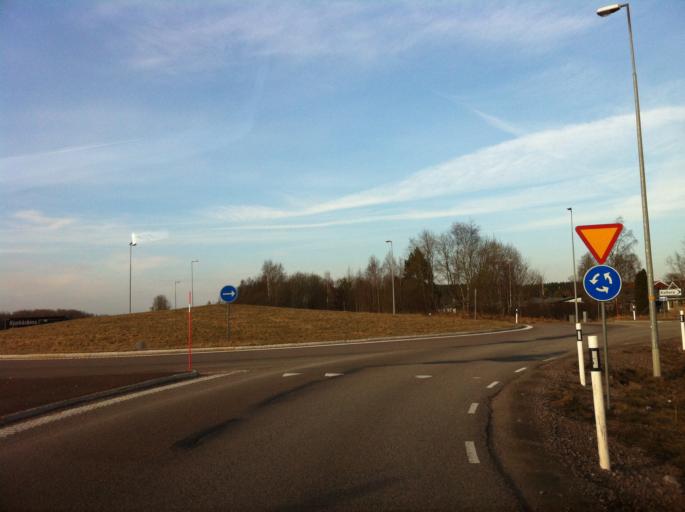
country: SE
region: Vaermland
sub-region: Storfors Kommun
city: Storfors
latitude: 59.5439
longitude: 14.2779
